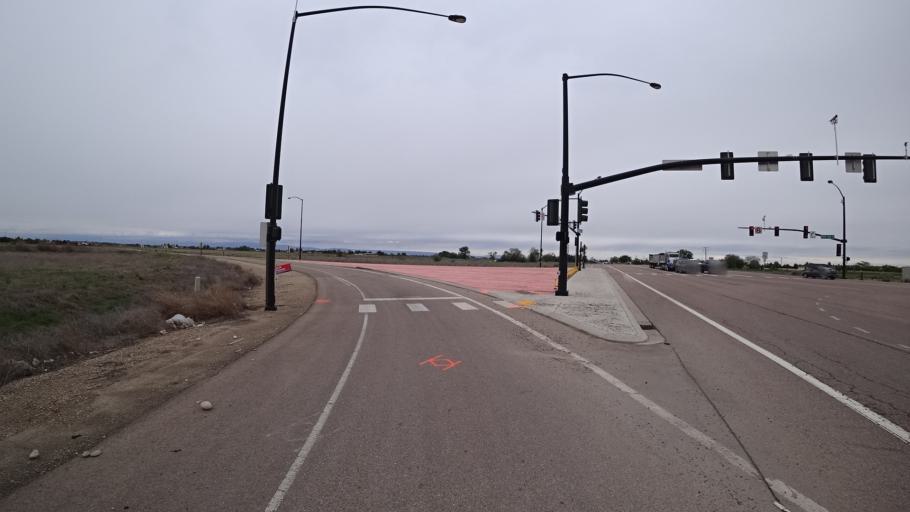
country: US
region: Idaho
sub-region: Ada County
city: Star
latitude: 43.6629
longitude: -116.4720
